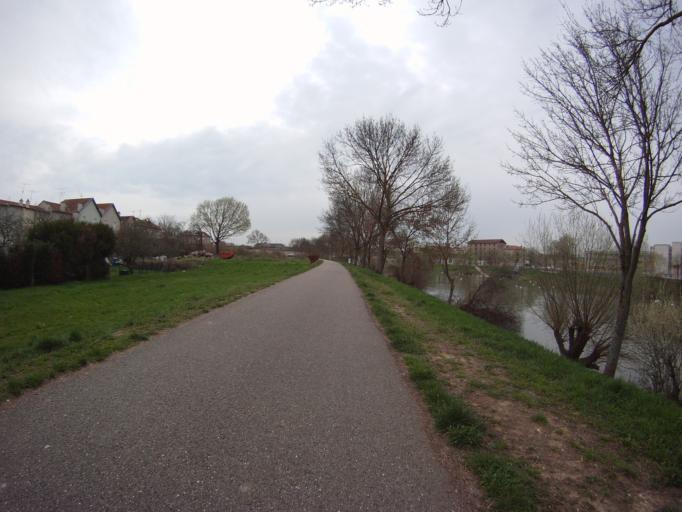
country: FR
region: Lorraine
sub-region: Departement de Meurthe-et-Moselle
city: Malzeville
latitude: 48.7072
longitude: 6.1821
